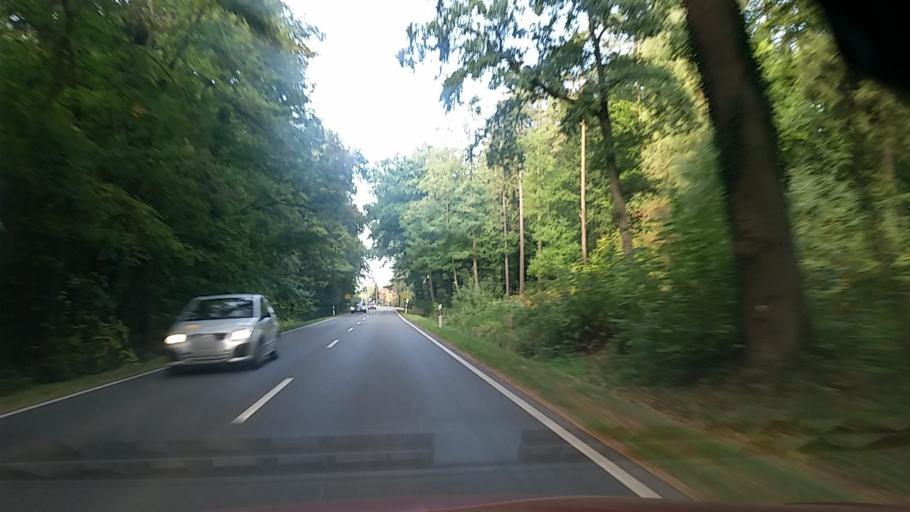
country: DE
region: Lower Saxony
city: Celle
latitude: 52.6232
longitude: 10.1367
